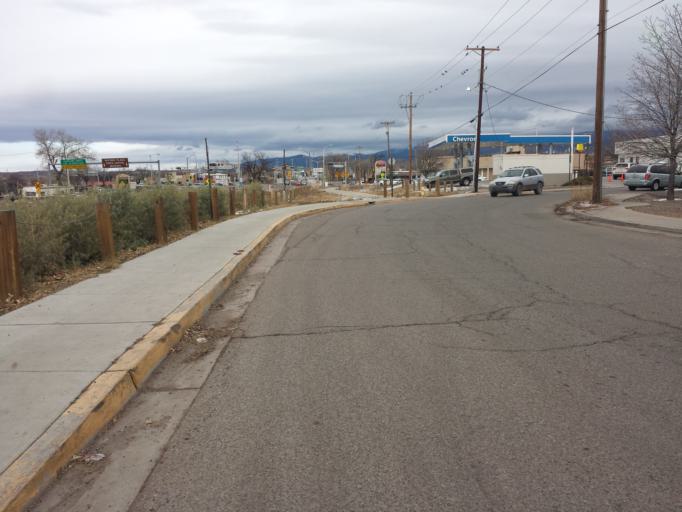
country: US
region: New Mexico
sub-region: Santa Fe County
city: Santa Fe
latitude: 35.6762
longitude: -105.9548
